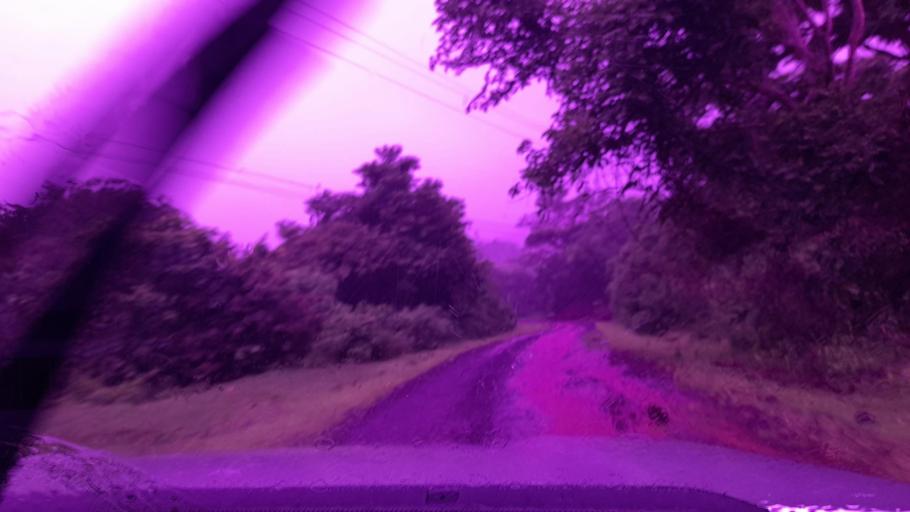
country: ET
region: Oromiya
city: Metu
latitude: 8.4735
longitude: 35.6393
